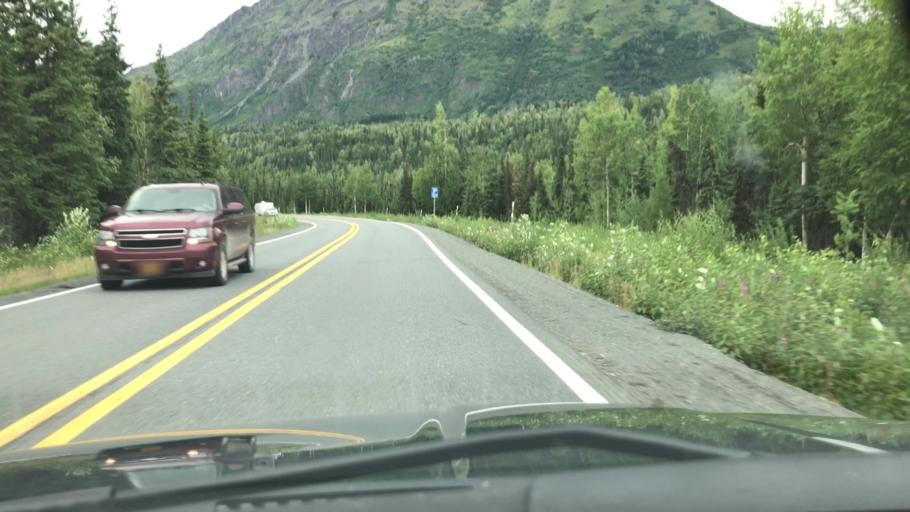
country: US
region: Alaska
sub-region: Kenai Peninsula Borough
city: Seward
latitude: 60.4855
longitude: -149.9624
